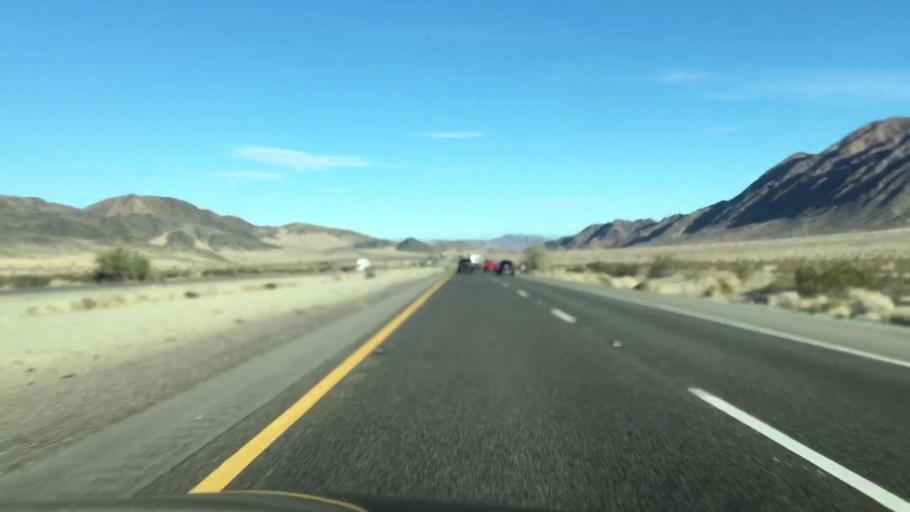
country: US
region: California
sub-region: San Bernardino County
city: Fort Irwin
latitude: 35.0866
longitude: -116.3575
